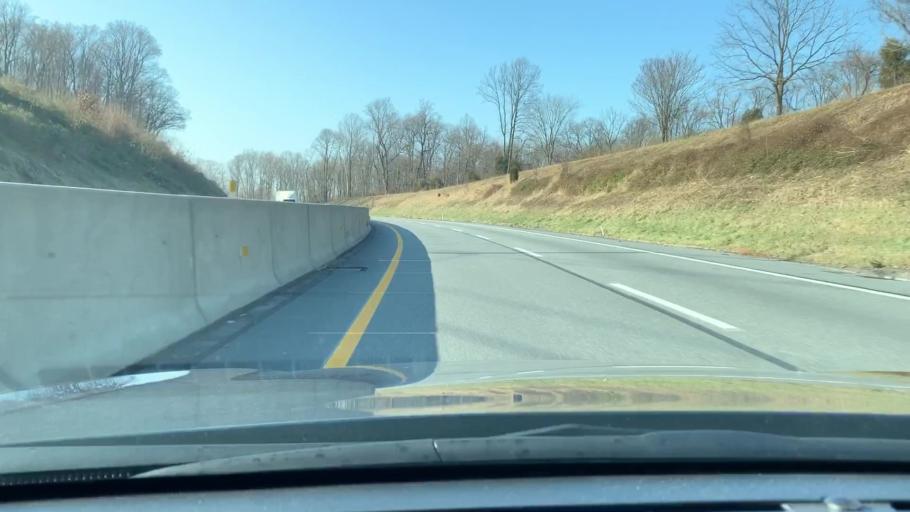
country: US
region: Pennsylvania
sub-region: Dauphin County
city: Middletown
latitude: 40.2091
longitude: -76.6583
